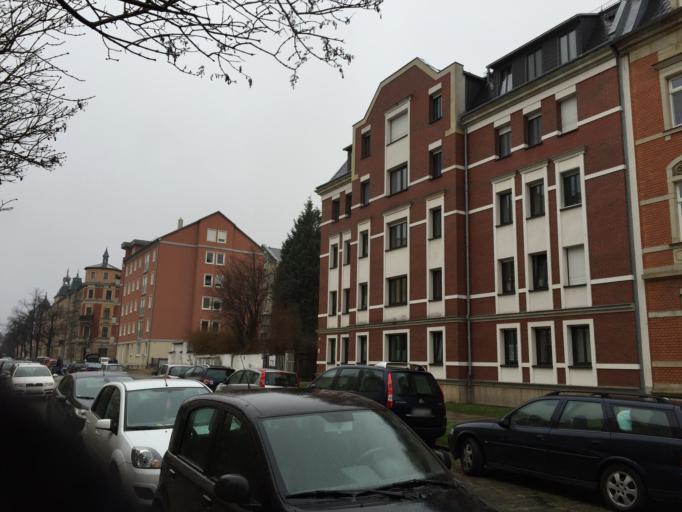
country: DE
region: Saxony
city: Dresden
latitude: 51.0401
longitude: 13.7004
